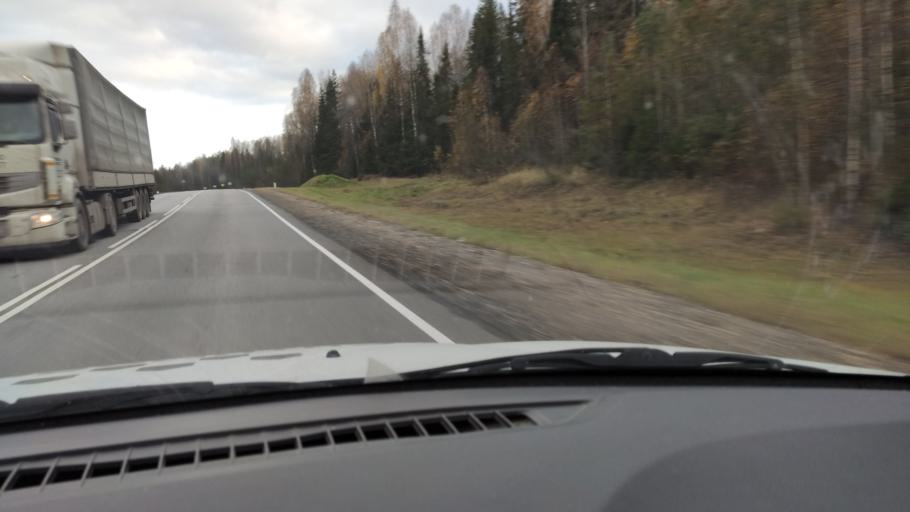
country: RU
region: Kirov
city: Chernaya Kholunitsa
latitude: 58.8339
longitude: 51.7572
